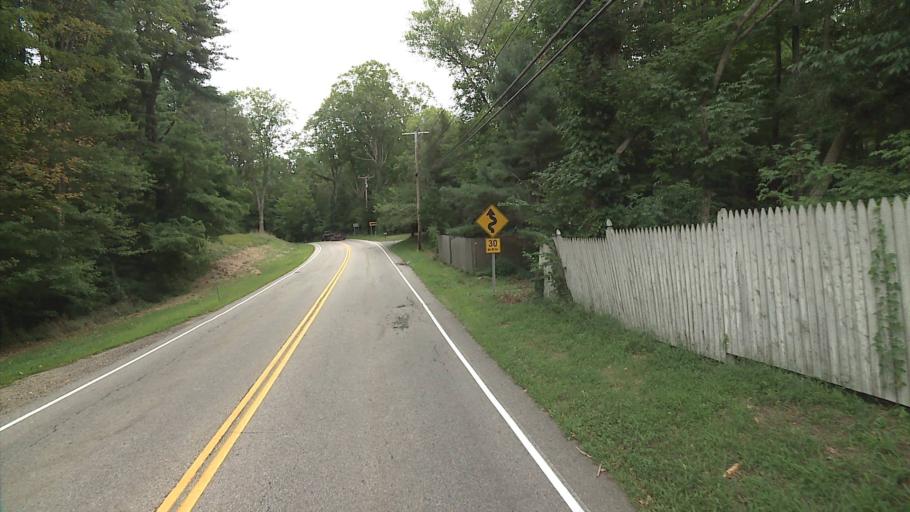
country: US
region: Connecticut
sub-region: Middlesex County
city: Essex Village
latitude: 41.3946
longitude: -72.3467
